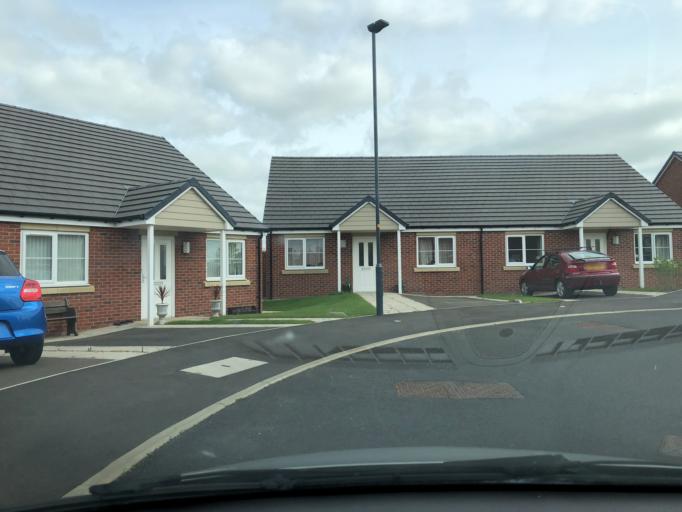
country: GB
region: England
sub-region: North Yorkshire
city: Thirsk
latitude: 54.2204
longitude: -1.3494
